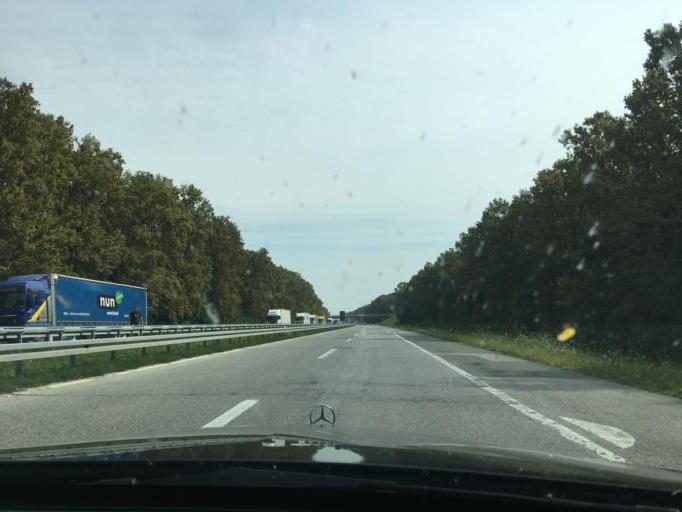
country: HR
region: Vukovarsko-Srijemska
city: Tovarnik
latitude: 45.0451
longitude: 19.1237
